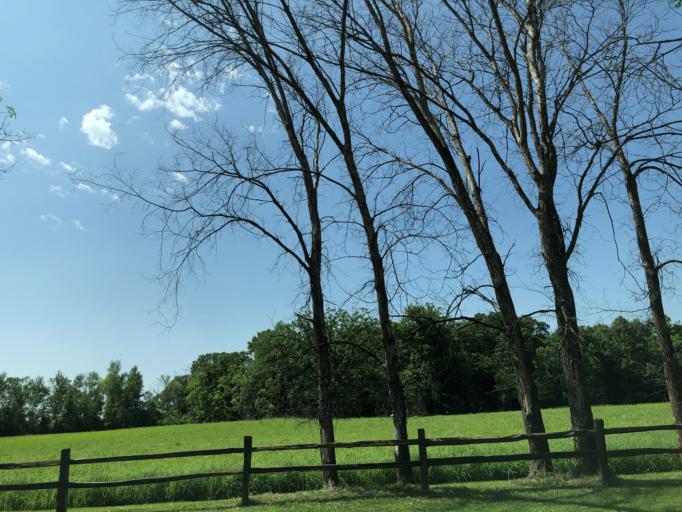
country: US
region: Minnesota
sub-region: Douglas County
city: Alexandria
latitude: 45.9412
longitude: -95.3762
